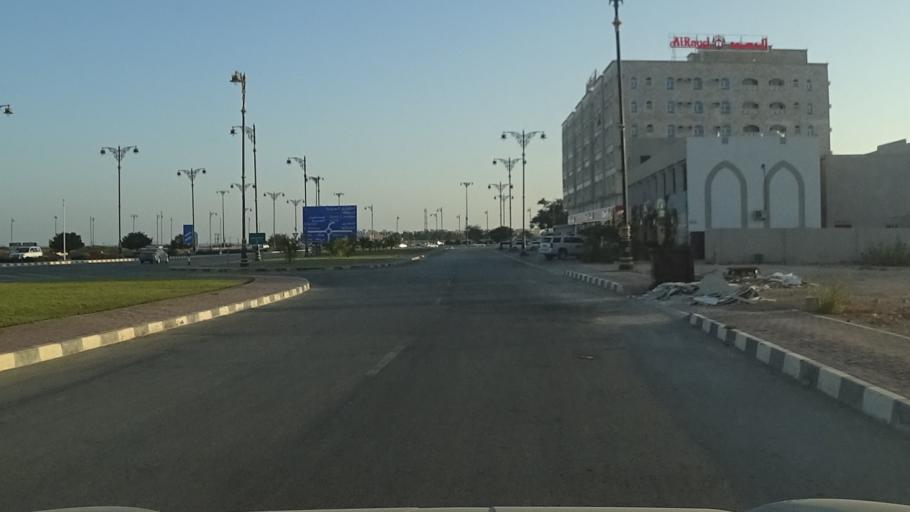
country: OM
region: Zufar
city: Salalah
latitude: 17.0286
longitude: 54.1721
